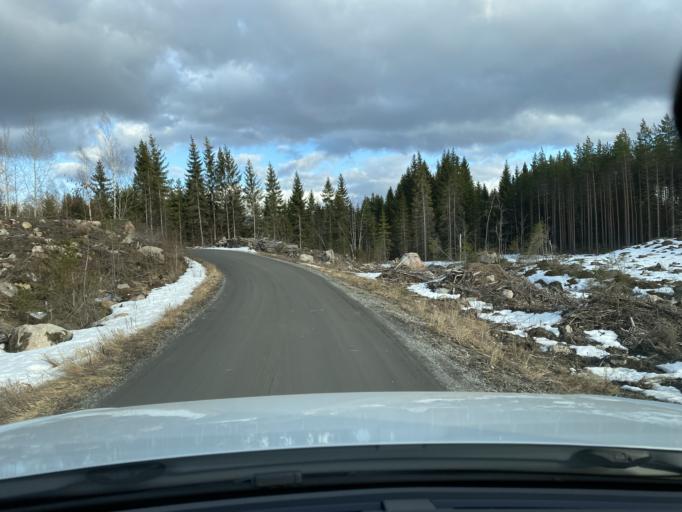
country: FI
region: Pirkanmaa
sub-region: Lounais-Pirkanmaa
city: Mouhijaervi
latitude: 61.4335
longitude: 22.9667
